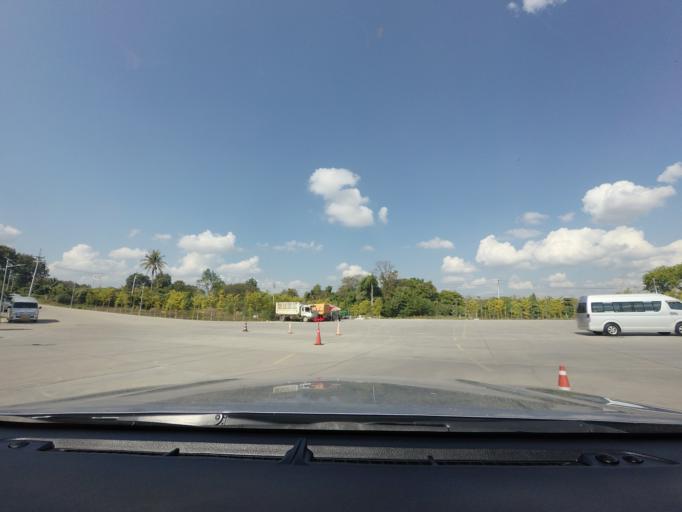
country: TH
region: Chiang Mai
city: Chai Prakan
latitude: 19.6571
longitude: 99.1473
